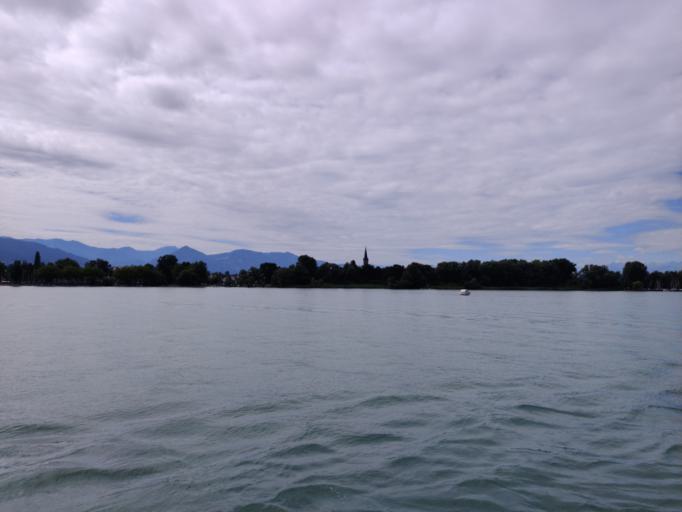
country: AT
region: Vorarlberg
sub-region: Politischer Bezirk Bregenz
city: Bregenz
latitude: 47.5109
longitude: 9.7237
